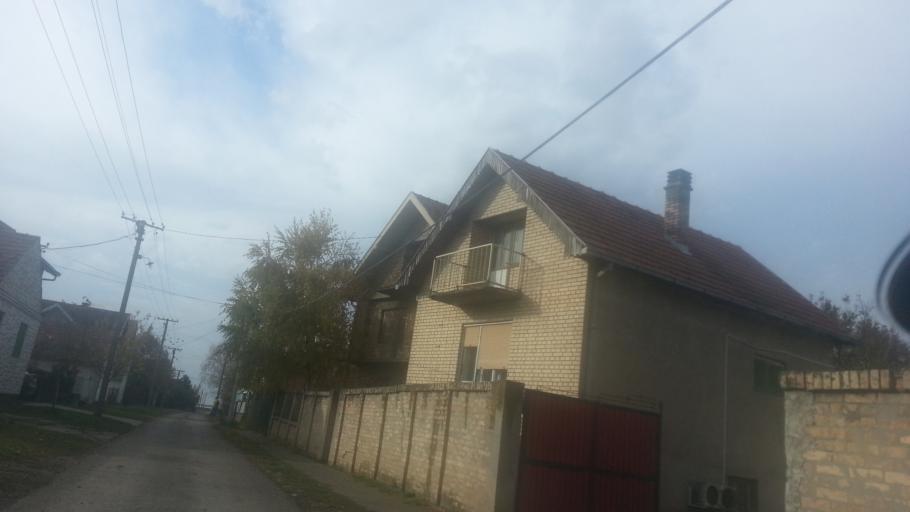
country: RS
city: Putinci
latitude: 44.9964
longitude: 19.9675
